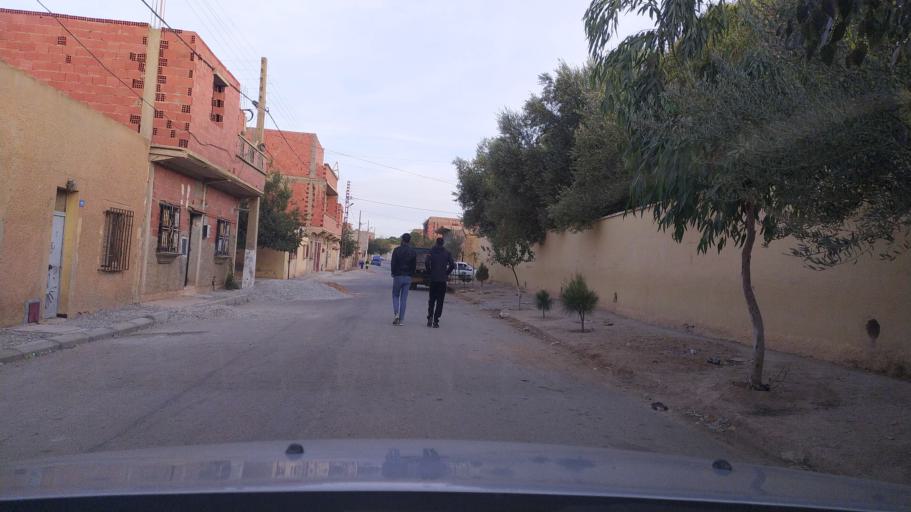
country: DZ
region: Tiaret
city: Frenda
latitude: 34.9000
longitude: 1.2353
